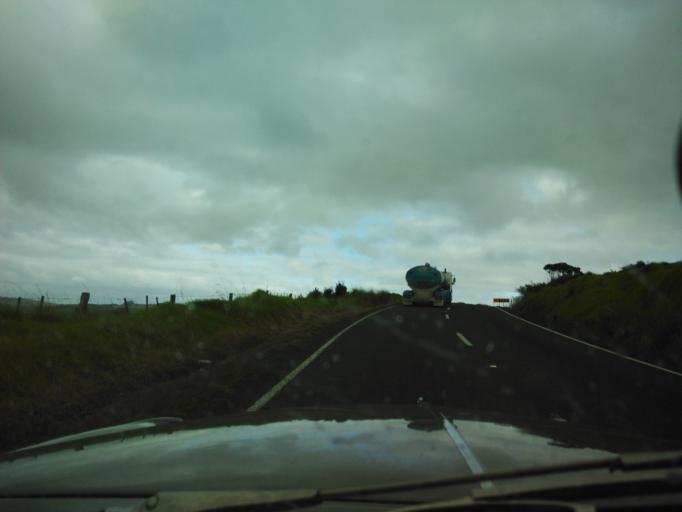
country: NZ
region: Auckland
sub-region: Auckland
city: Wellsford
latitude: -36.1435
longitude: 174.4985
